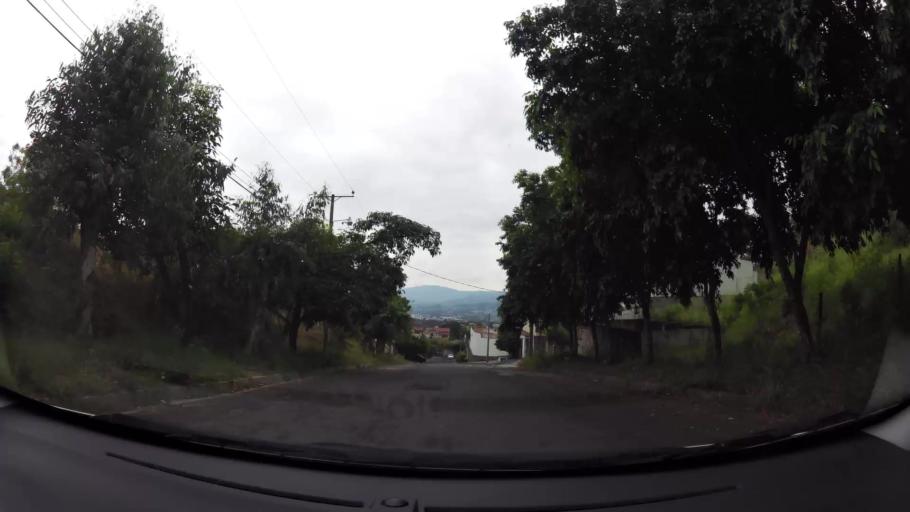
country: SV
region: San Salvador
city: Mejicanos
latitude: 13.7189
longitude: -89.2472
